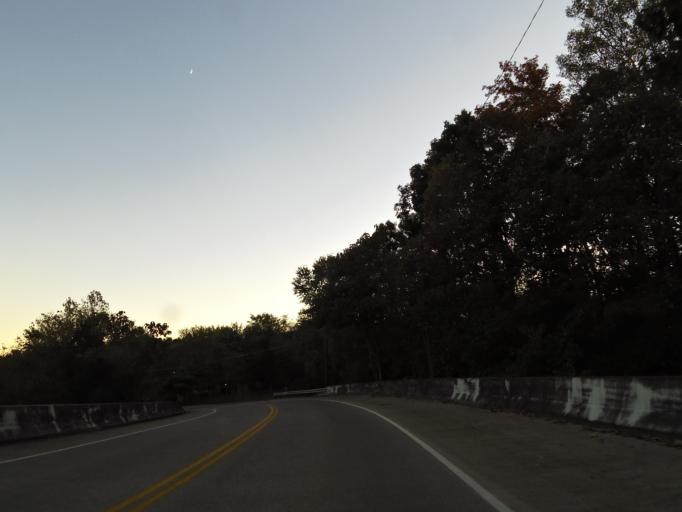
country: US
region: Tennessee
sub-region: Knox County
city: Knoxville
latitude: 36.0206
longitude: -83.9763
